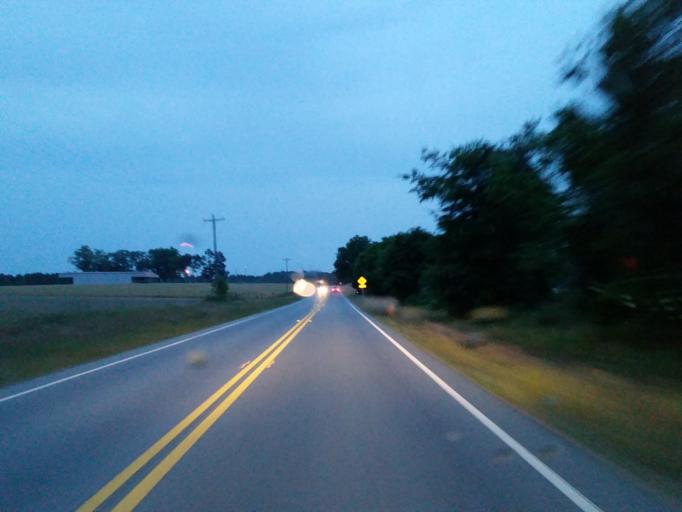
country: US
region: Georgia
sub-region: Turner County
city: Ashburn
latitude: 31.5944
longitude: -83.5831
